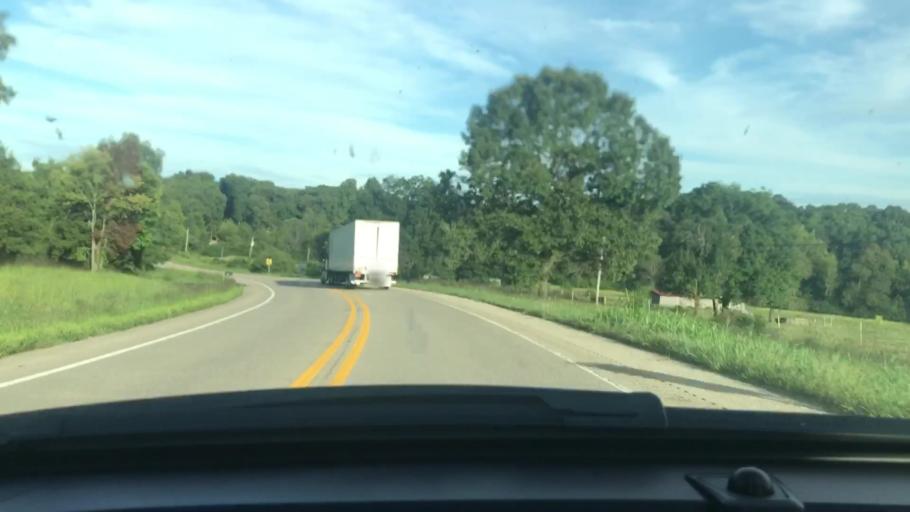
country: US
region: Arkansas
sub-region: Randolph County
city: Pocahontas
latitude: 36.2125
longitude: -91.2125
